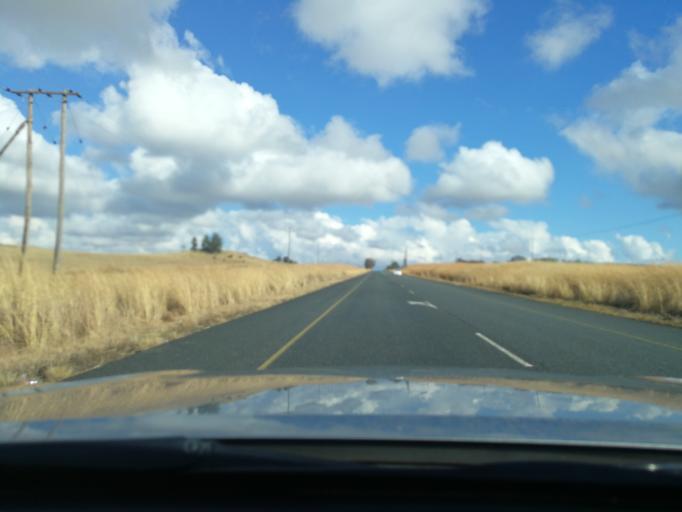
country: ZA
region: Orange Free State
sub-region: Thabo Mofutsanyana District Municipality
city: Reitz
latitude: -27.9943
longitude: 28.3755
